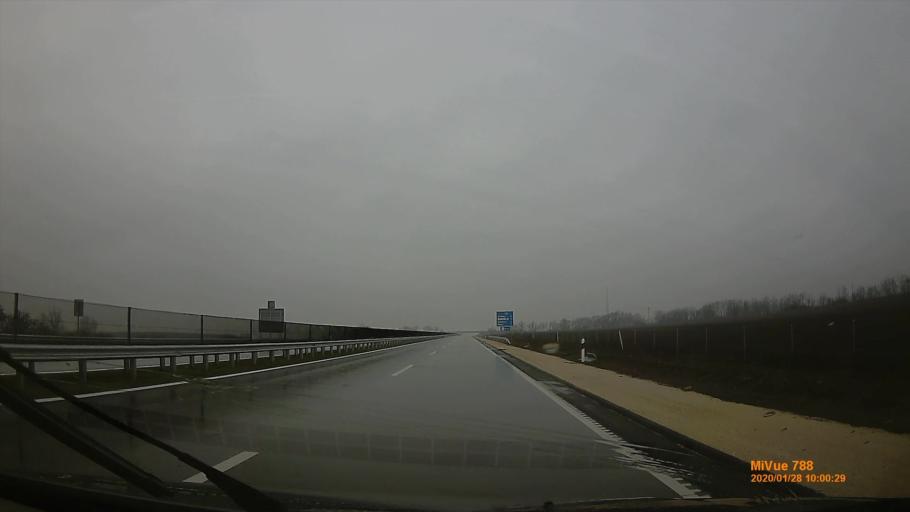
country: HU
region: Pest
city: Albertirsa
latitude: 47.2652
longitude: 19.6146
